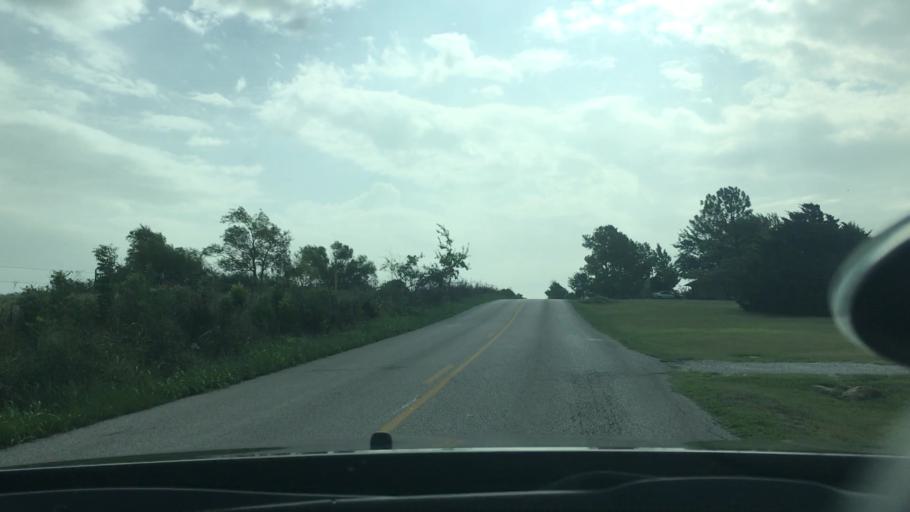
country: US
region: Oklahoma
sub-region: Carter County
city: Lone Grove
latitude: 34.2020
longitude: -97.2203
